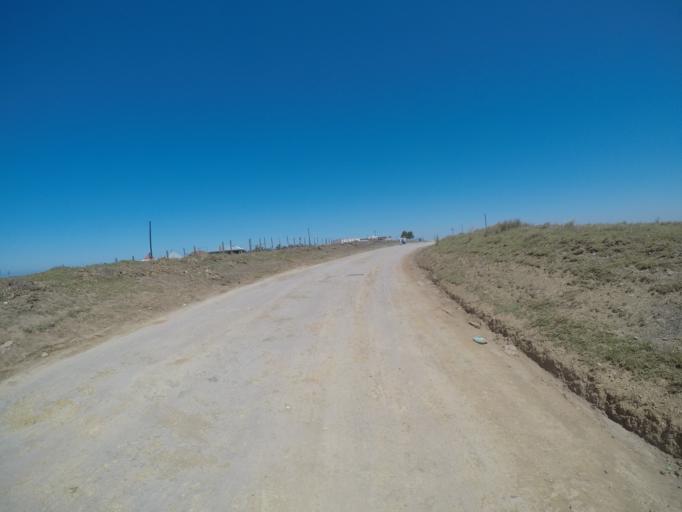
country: ZA
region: Eastern Cape
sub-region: OR Tambo District Municipality
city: Libode
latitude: -31.9443
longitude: 29.0273
